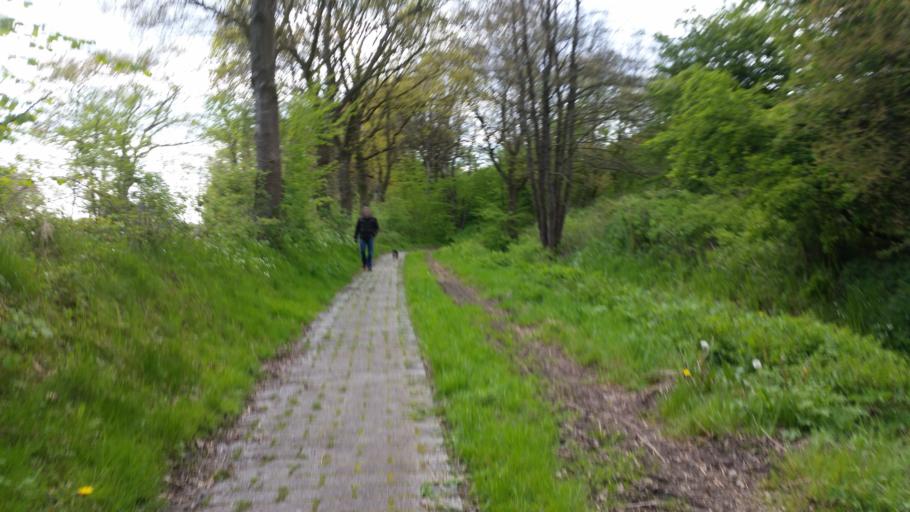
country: DE
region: Lower Saxony
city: Aurich
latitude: 53.4549
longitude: 7.4920
